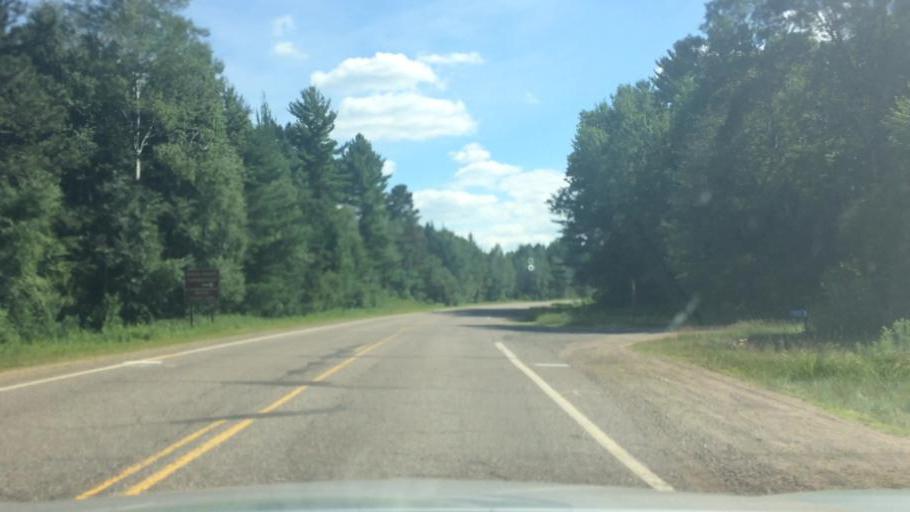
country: US
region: Wisconsin
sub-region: Vilas County
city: Lac du Flambeau
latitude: 46.0649
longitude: -89.6451
